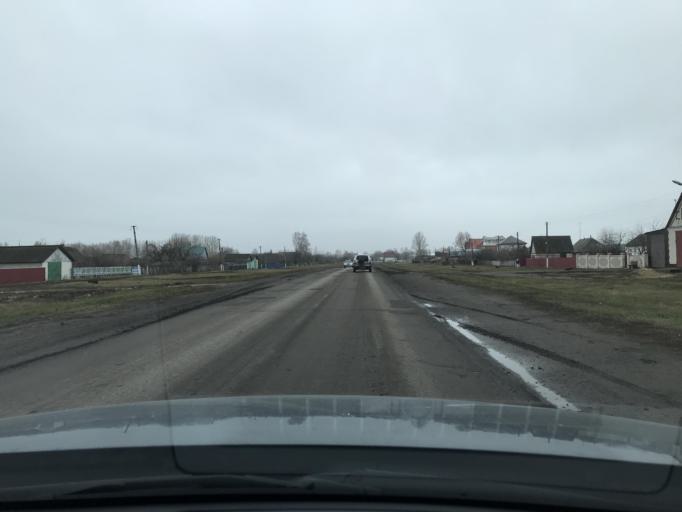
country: RU
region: Penza
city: Zemetchino
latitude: 53.5042
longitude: 42.6337
